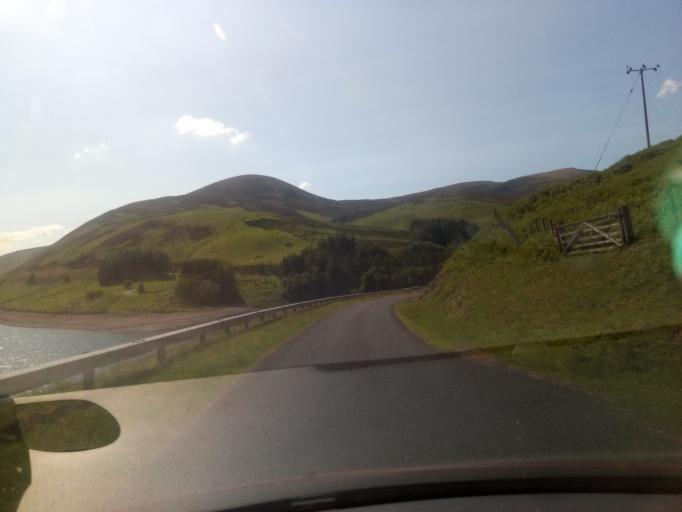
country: GB
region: Scotland
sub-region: The Scottish Borders
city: Peebles
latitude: 55.4933
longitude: -3.2690
